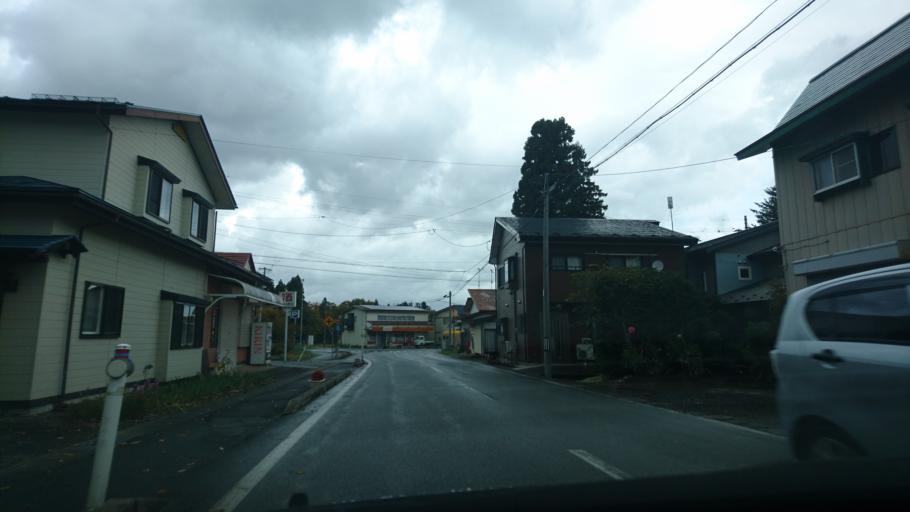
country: JP
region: Iwate
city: Shizukuishi
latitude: 39.6477
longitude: 140.9516
